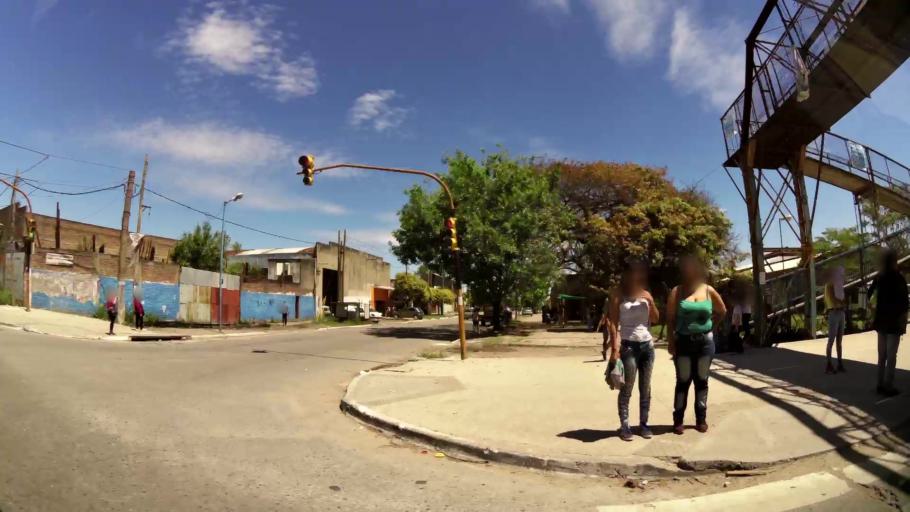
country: AR
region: Buenos Aires
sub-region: Partido de Quilmes
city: Quilmes
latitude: -34.7334
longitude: -58.3251
